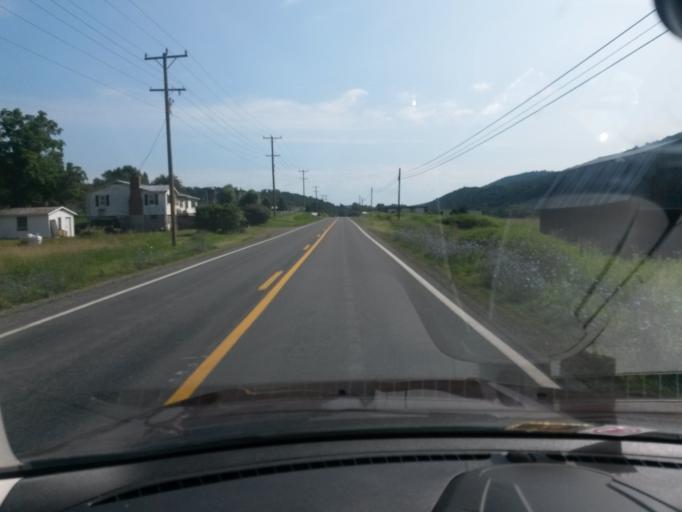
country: US
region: Virginia
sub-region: Shenandoah County
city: Basye
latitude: 38.9747
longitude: -78.7962
